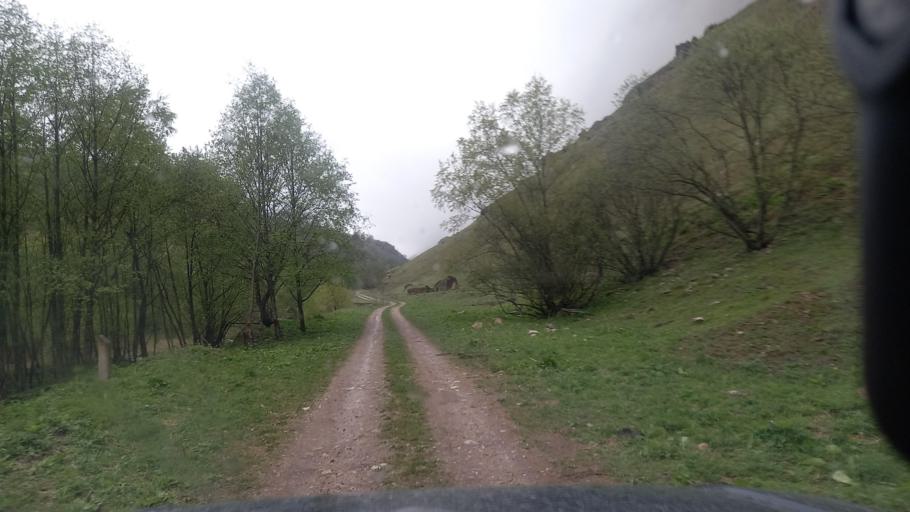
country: RU
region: Kabardino-Balkariya
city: Bylym
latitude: 43.5961
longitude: 42.9588
